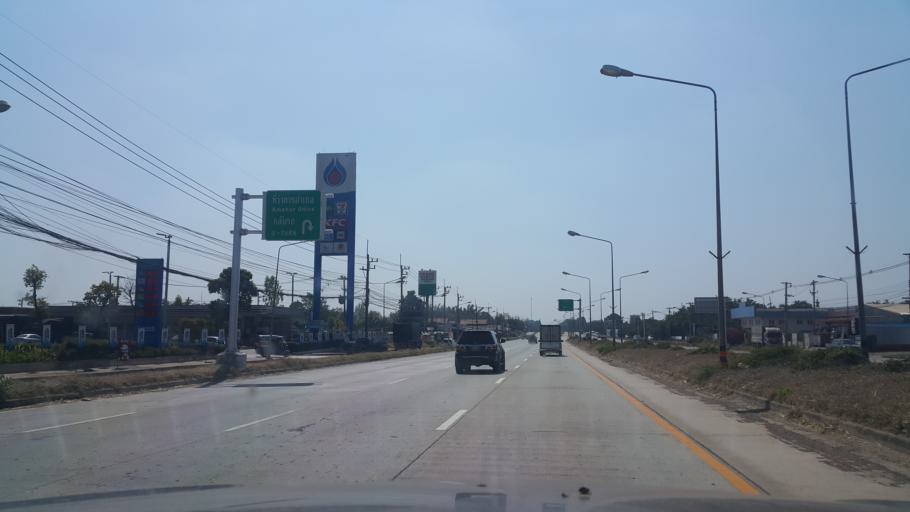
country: TH
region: Changwat Udon Thani
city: Non Sa-at
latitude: 16.8479
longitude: 102.8550
